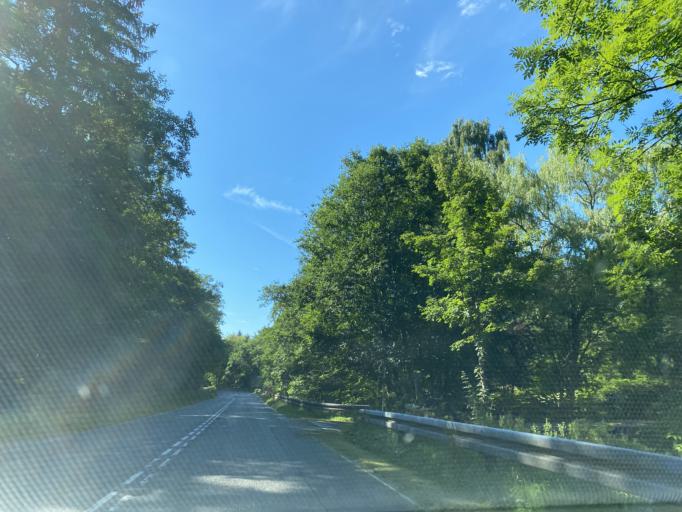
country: DK
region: South Denmark
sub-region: Vejle Kommune
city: Vejle
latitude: 55.7576
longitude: 9.5282
